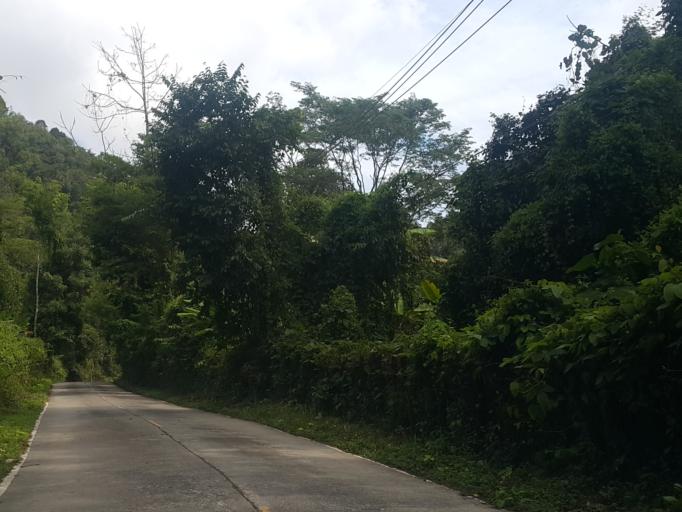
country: TH
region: Chiang Mai
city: Mae On
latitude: 18.8759
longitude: 99.3364
